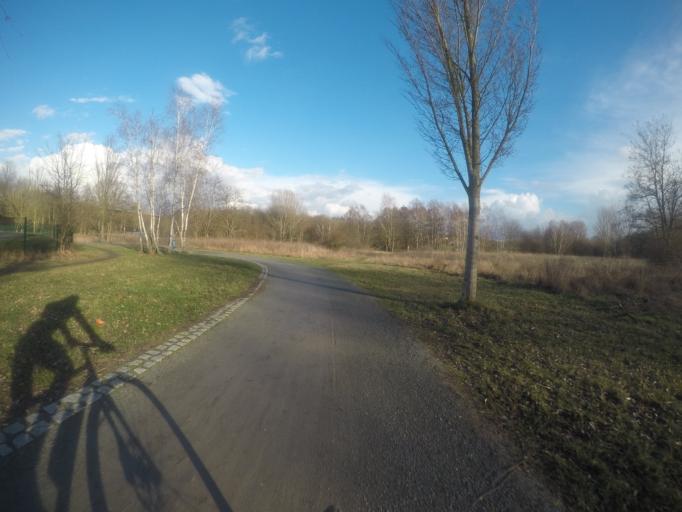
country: DE
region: Berlin
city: Kaulsdorf
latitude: 52.5114
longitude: 13.5717
